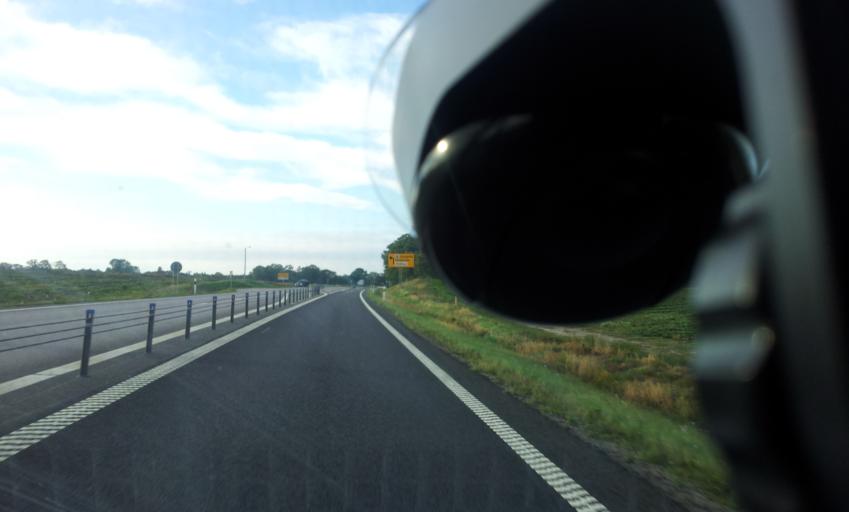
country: SE
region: Kalmar
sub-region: Kalmar Kommun
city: Lindsdal
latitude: 56.8125
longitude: 16.3687
